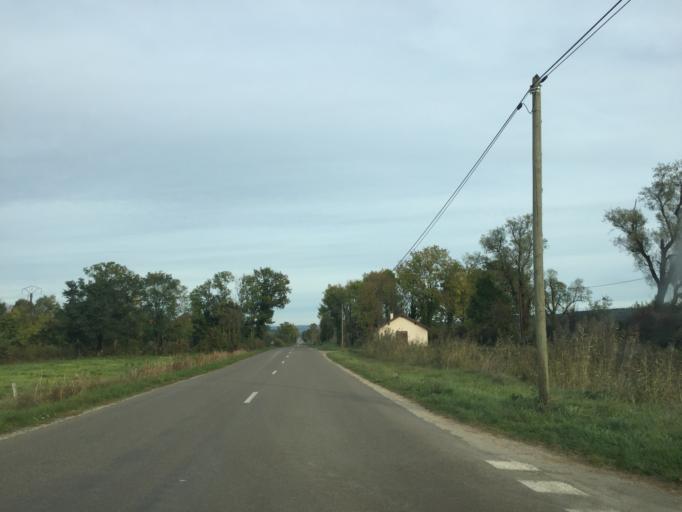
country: FR
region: Franche-Comte
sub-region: Departement du Jura
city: Orgelet
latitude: 46.5269
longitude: 5.5506
